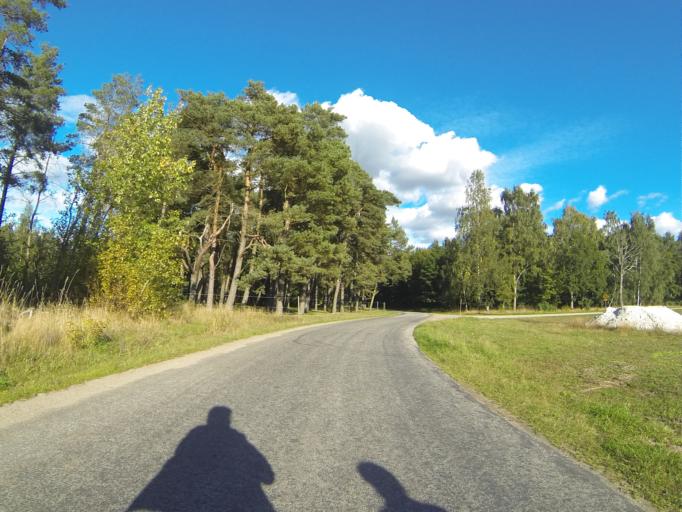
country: SE
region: Skane
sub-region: Eslovs Kommun
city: Eslov
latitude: 55.7327
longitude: 13.3634
